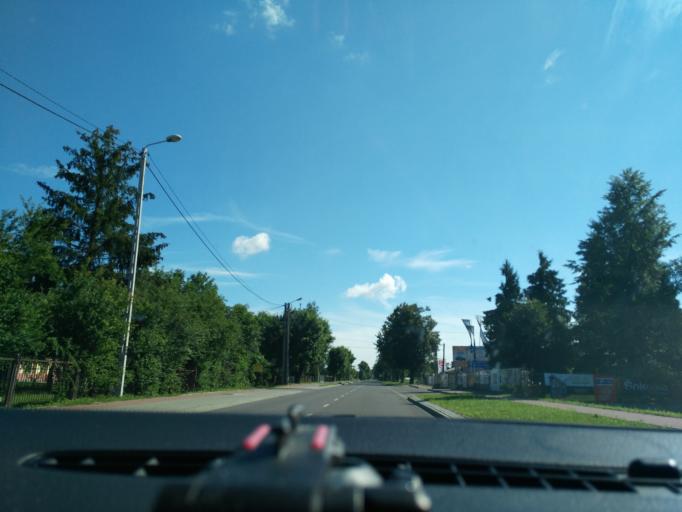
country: PL
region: Lublin Voivodeship
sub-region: Powiat radzynski
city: Radzyn Podlaski
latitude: 51.7934
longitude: 22.6296
